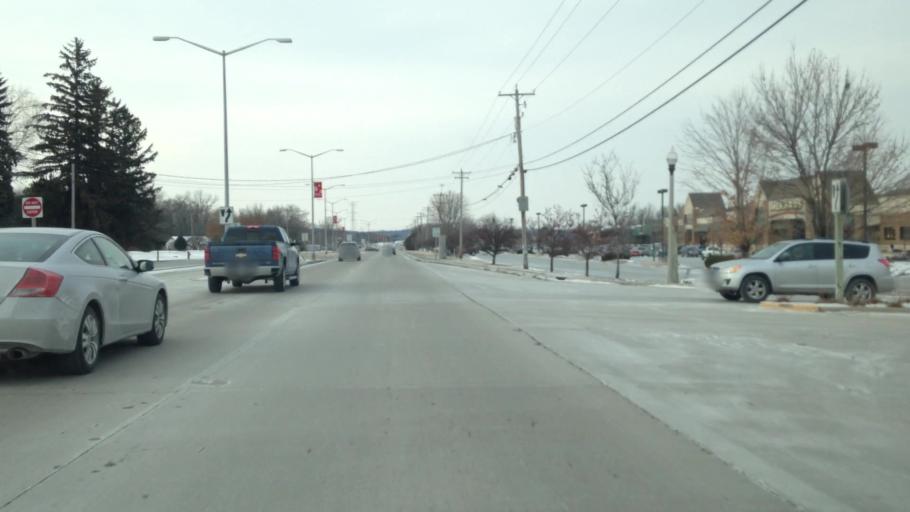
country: US
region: Wisconsin
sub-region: Waukesha County
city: Menomonee Falls
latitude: 43.1937
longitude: -88.1388
